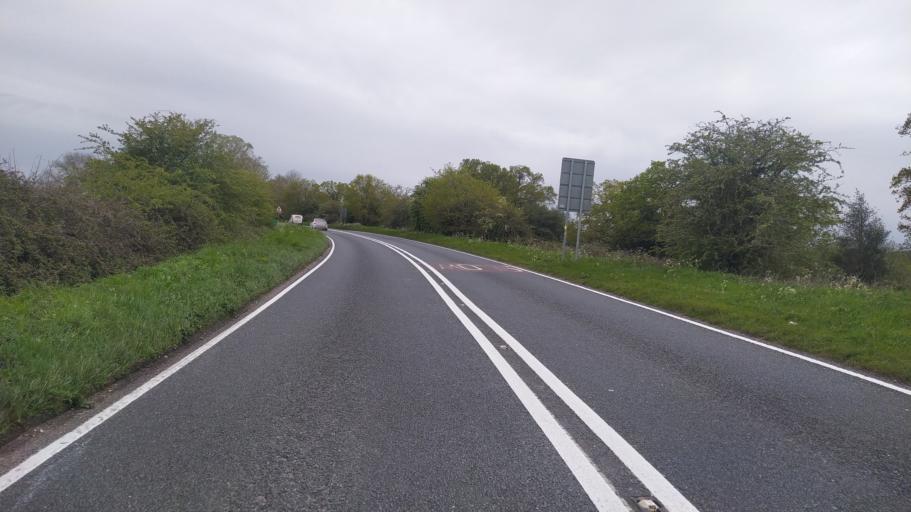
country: GB
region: England
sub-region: Hampshire
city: Fordingbridge
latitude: 50.8931
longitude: -1.7855
